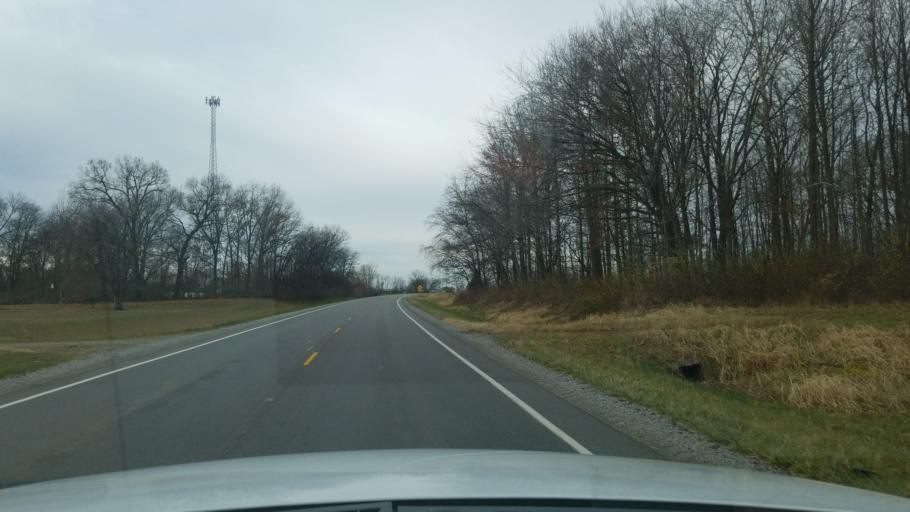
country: US
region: Illinois
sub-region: White County
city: Carmi
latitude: 37.9095
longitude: -88.1348
